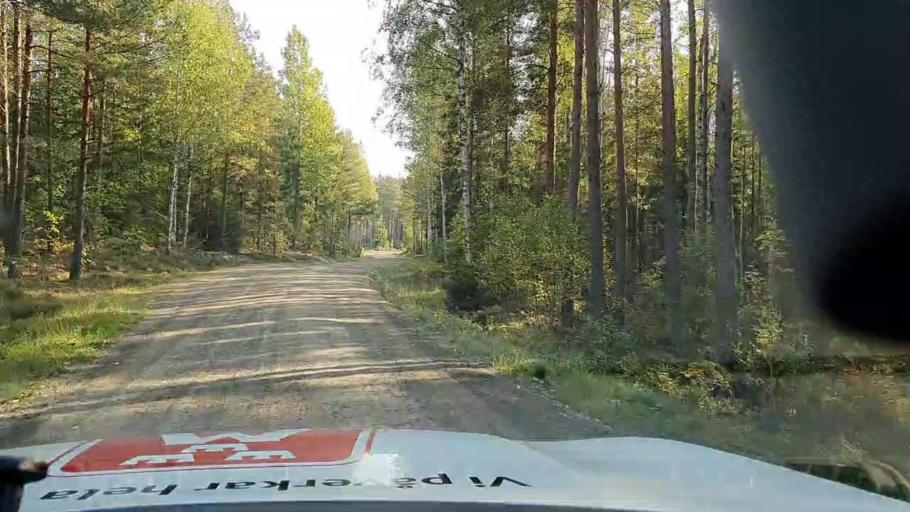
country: SE
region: Soedermanland
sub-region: Eskilstuna Kommun
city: Kvicksund
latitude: 59.3307
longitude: 16.2255
